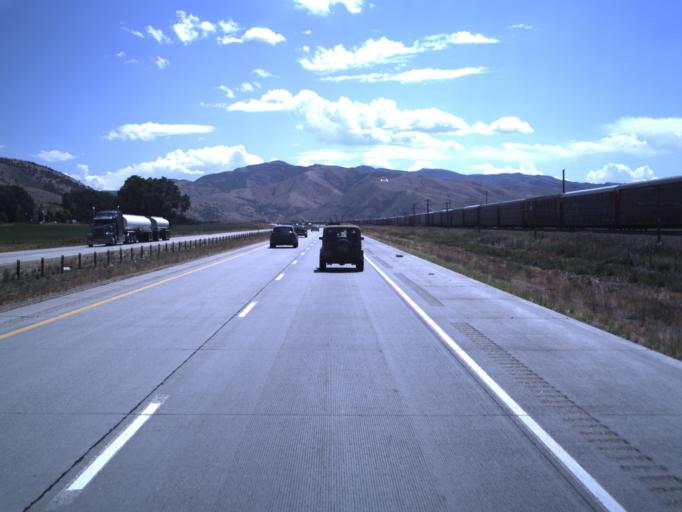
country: US
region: Utah
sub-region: Morgan County
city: Morgan
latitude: 41.0625
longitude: -111.7059
